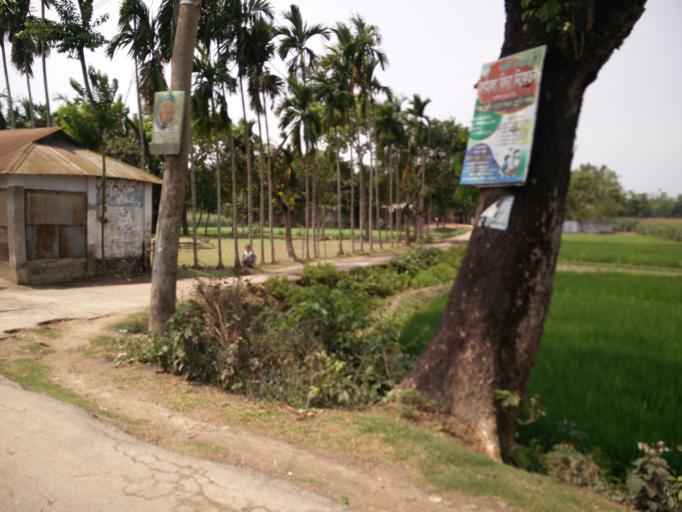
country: BD
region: Dhaka
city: Sherpur
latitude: 24.9513
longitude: 90.1639
